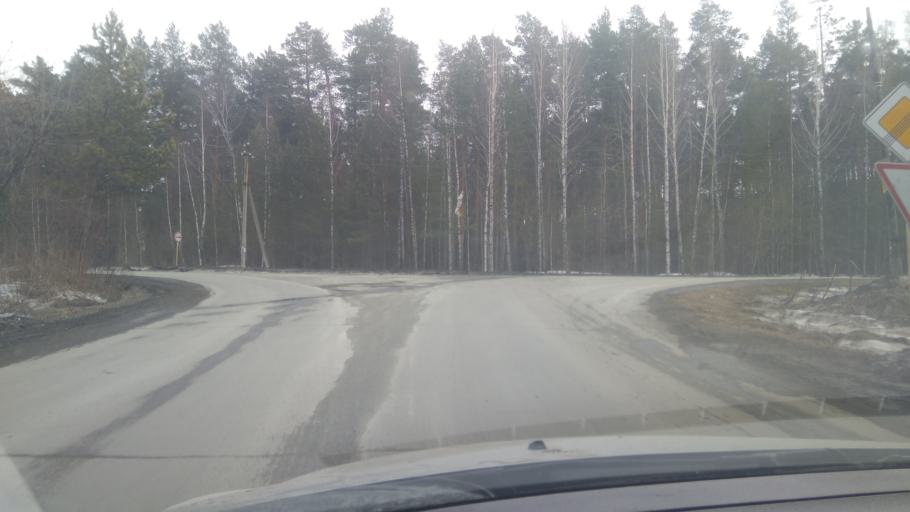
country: RU
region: Sverdlovsk
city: Severka
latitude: 56.8335
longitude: 60.3853
